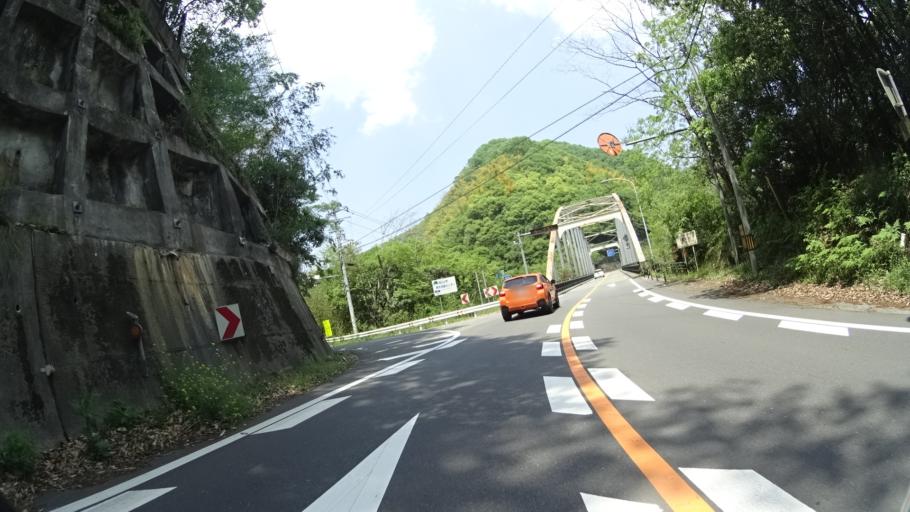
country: JP
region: Ehime
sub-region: Shikoku-chuo Shi
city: Matsuyama
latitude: 33.8894
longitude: 132.8354
